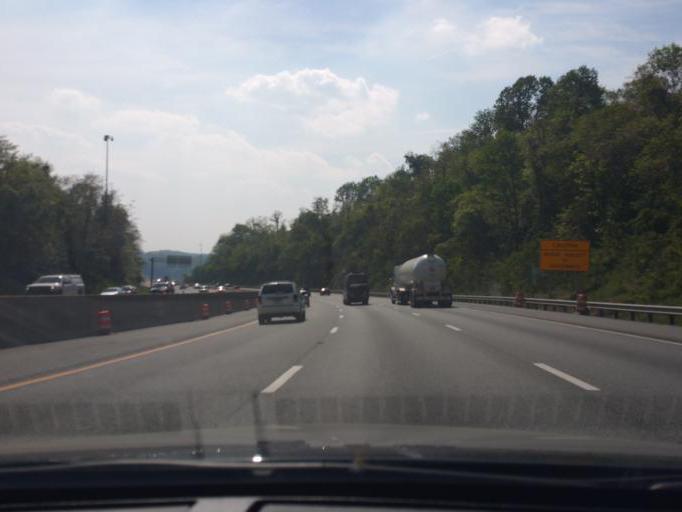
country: US
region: Maryland
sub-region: Cecil County
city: Perryville
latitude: 39.5858
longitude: -76.0928
